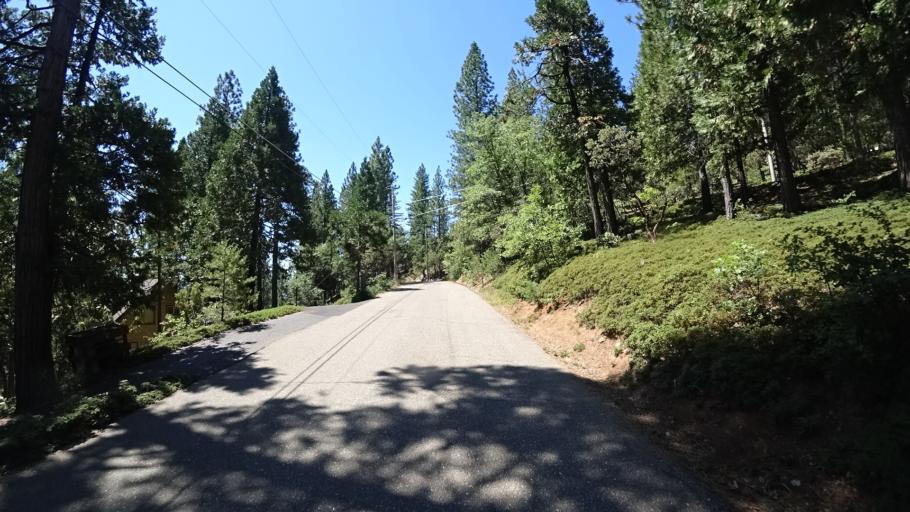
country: US
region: California
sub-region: Calaveras County
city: Arnold
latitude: 38.2267
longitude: -120.3752
